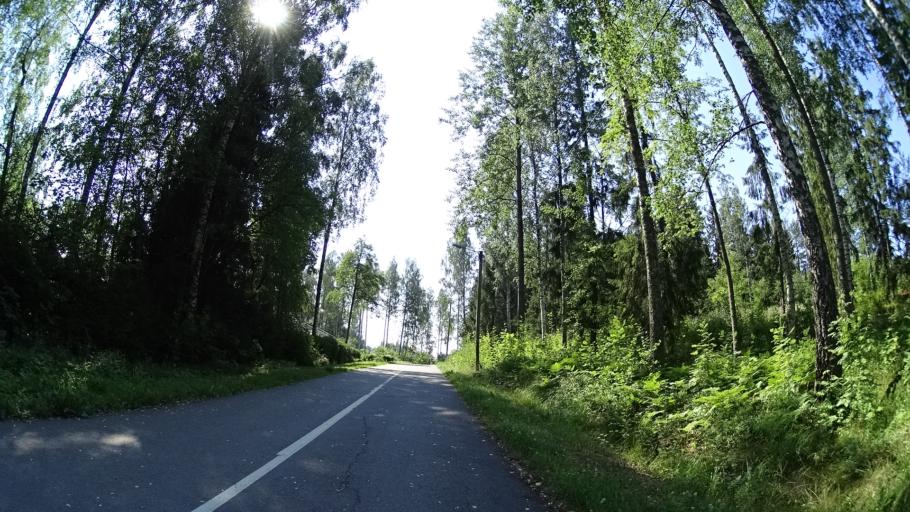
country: FI
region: Uusimaa
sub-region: Helsinki
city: Kerava
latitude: 60.3874
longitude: 25.0939
